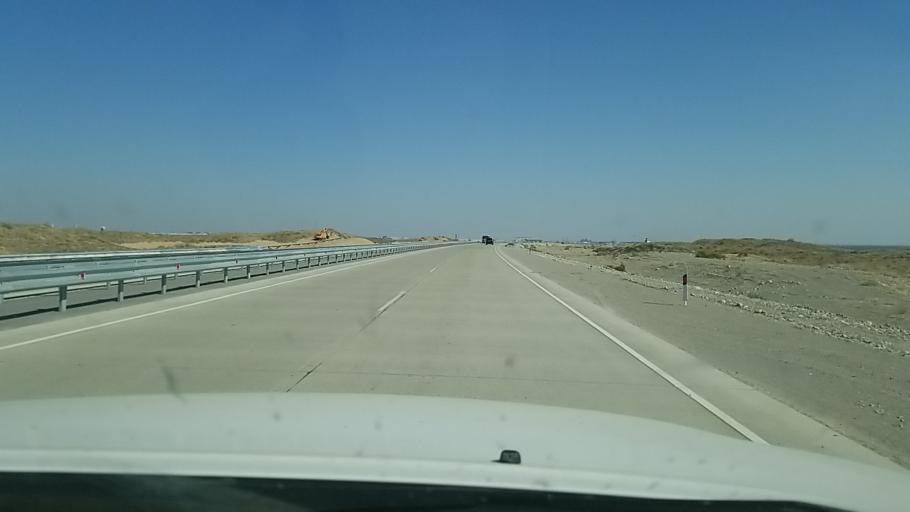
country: KZ
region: Almaty Oblysy
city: Zharkent
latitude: 44.1736
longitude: 80.3387
